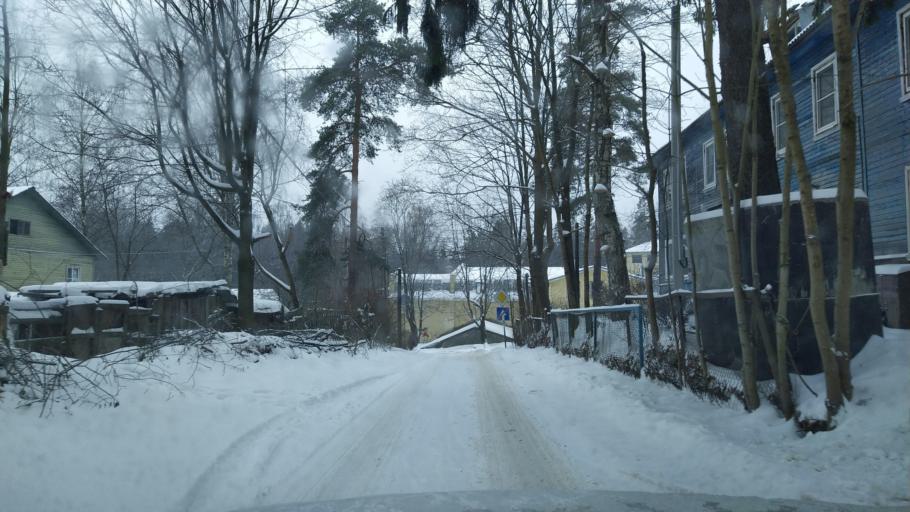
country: RU
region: Leningrad
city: Vsevolozhsk
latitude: 60.0204
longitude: 30.6712
